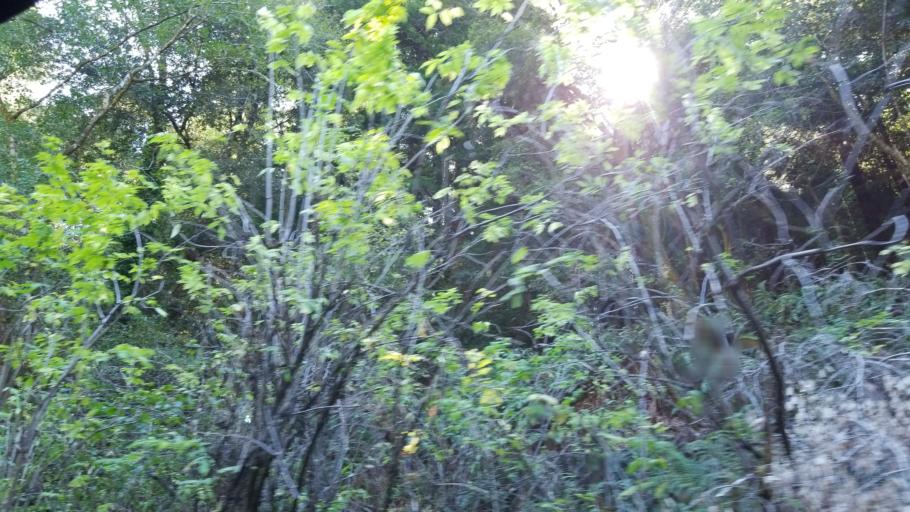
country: US
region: California
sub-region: Mendocino County
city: Fort Bragg
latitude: 39.4488
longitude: -123.7840
